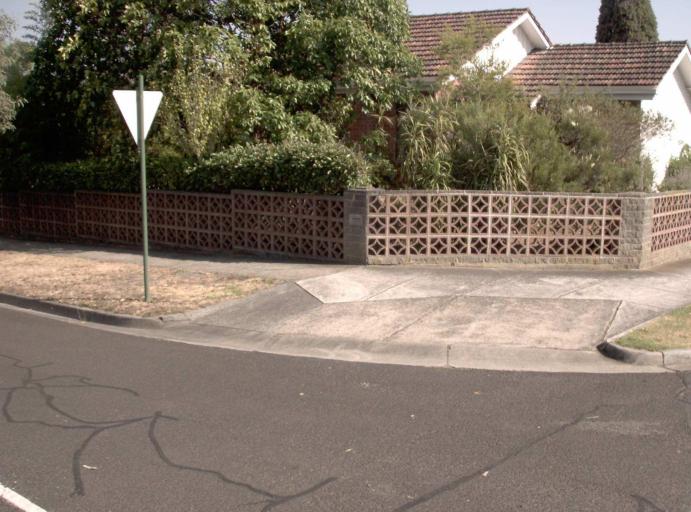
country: AU
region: Victoria
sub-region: Whitehorse
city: Box Hill North
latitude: -37.8026
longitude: 145.1266
